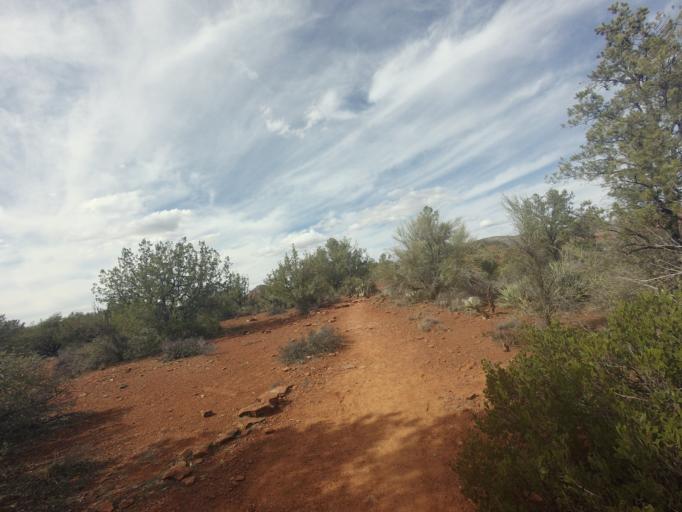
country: US
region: Arizona
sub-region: Yavapai County
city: West Sedona
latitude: 34.8074
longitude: -111.8324
